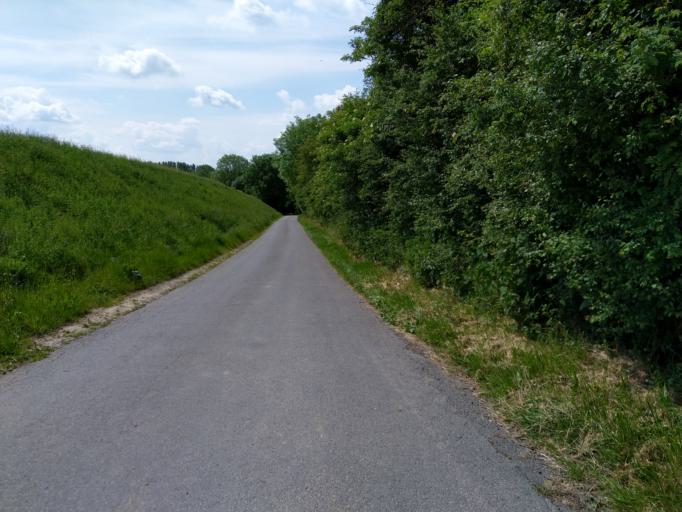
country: FR
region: Nord-Pas-de-Calais
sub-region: Departement du Nord
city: Le Quesnoy
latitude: 50.2651
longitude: 3.6512
